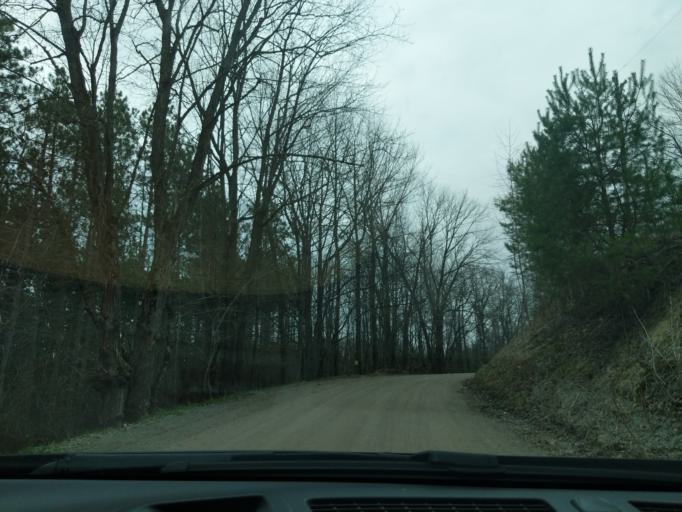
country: CA
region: Ontario
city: Orangeville
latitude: 44.0037
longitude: -80.0165
